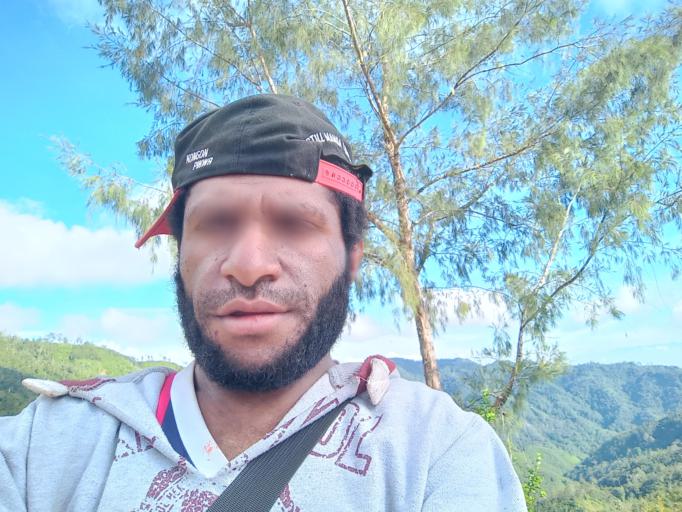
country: PG
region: Jiwaka
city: Minj
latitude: -5.6869
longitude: 144.6472
